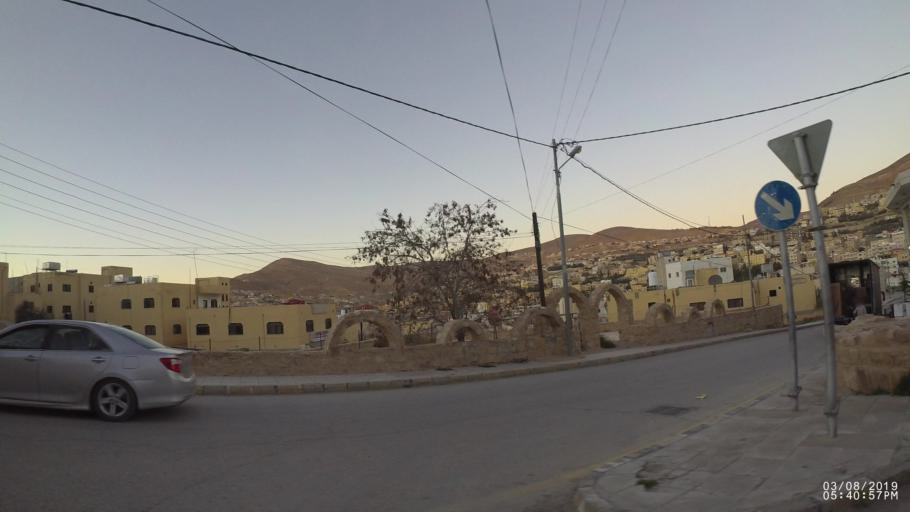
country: JO
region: Ma'an
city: Petra
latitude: 30.3206
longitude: 35.4745
